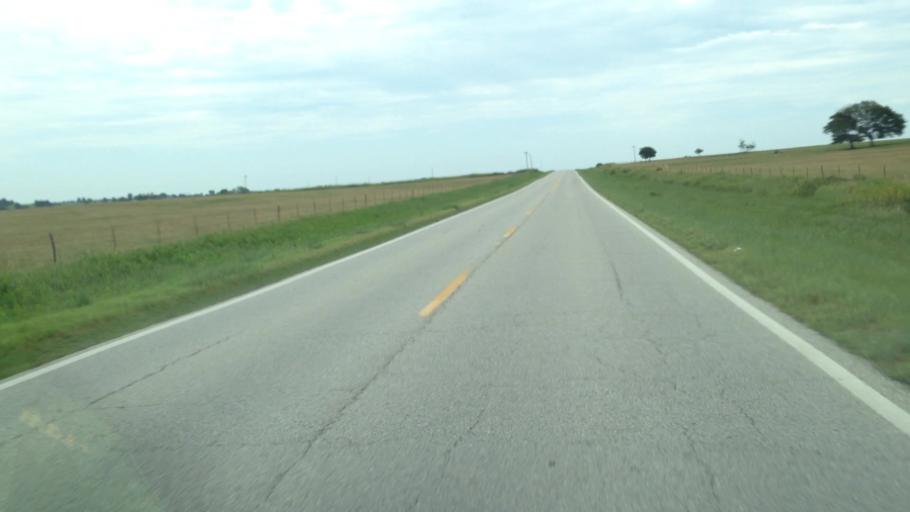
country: US
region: Kansas
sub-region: Labette County
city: Chetopa
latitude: 36.8413
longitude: -95.1281
